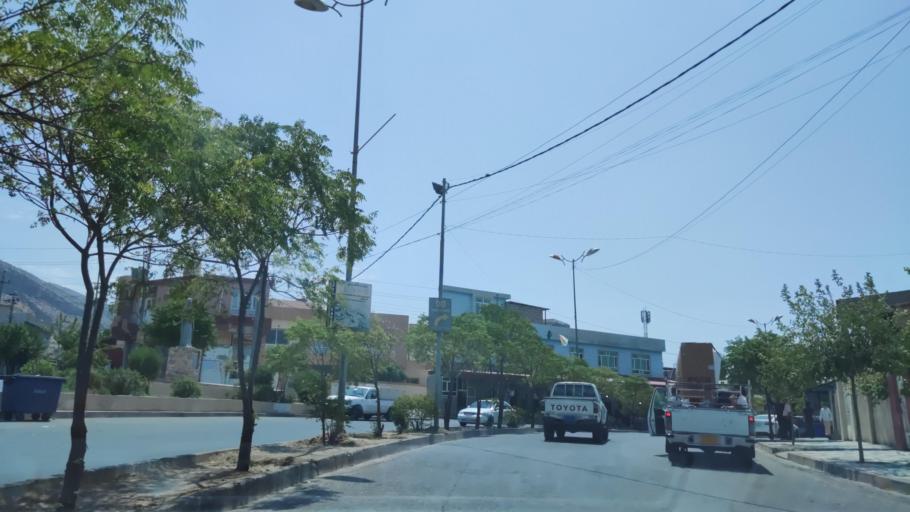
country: IQ
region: Arbil
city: Shaqlawah
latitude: 36.5518
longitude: 44.3548
